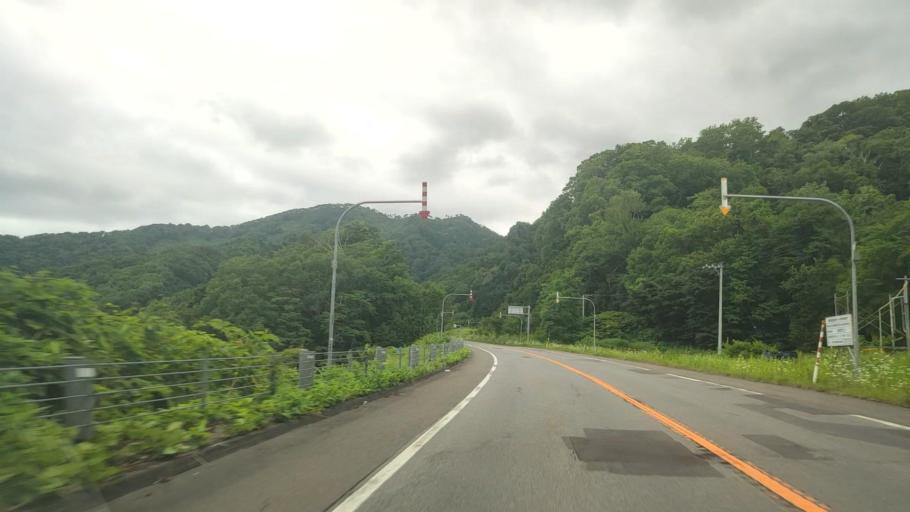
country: JP
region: Hokkaido
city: Niseko Town
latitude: 42.6040
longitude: 140.5671
